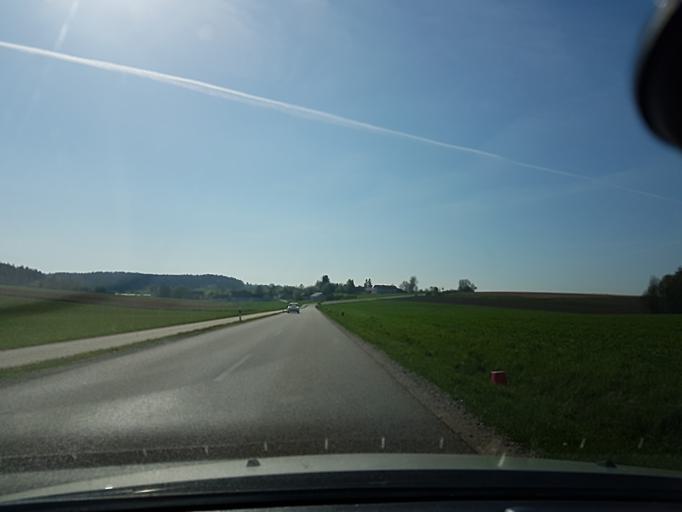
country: DE
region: Bavaria
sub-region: Lower Bavaria
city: Furth
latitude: 48.4168
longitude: 12.3671
